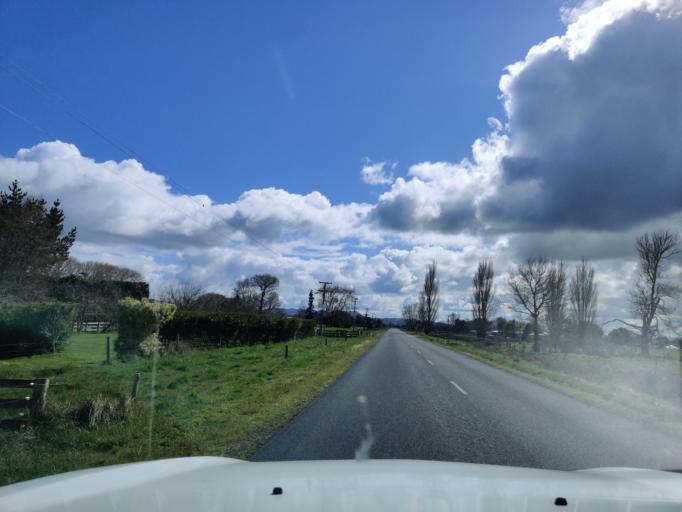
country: NZ
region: Waikato
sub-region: Waikato District
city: Ngaruawahia
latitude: -37.5998
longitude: 175.2993
